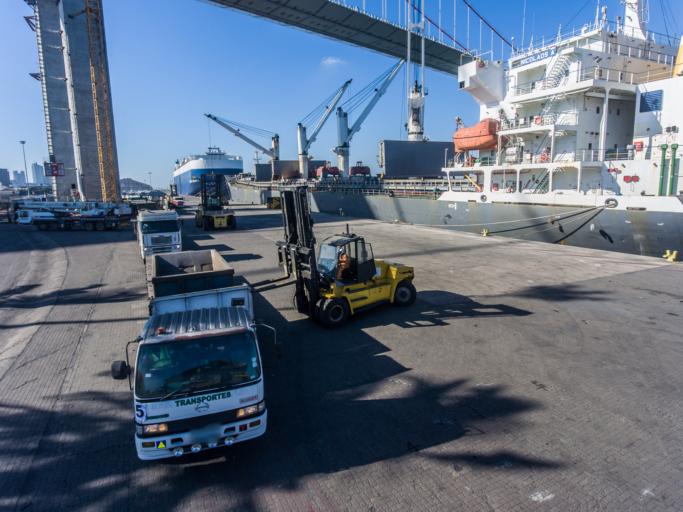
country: MZ
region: Maputo City
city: Maputo
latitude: -25.9693
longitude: 32.5575
